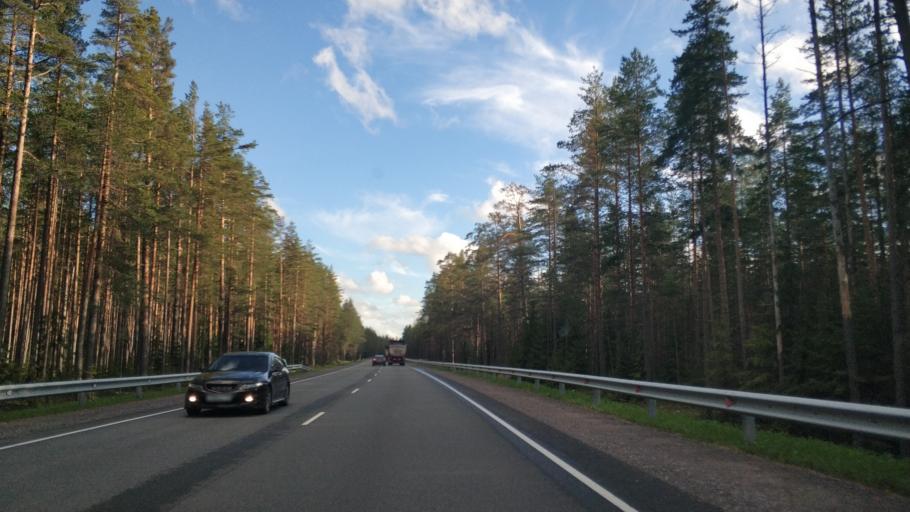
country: RU
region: Leningrad
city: Priozersk
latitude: 60.8909
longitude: 30.1597
